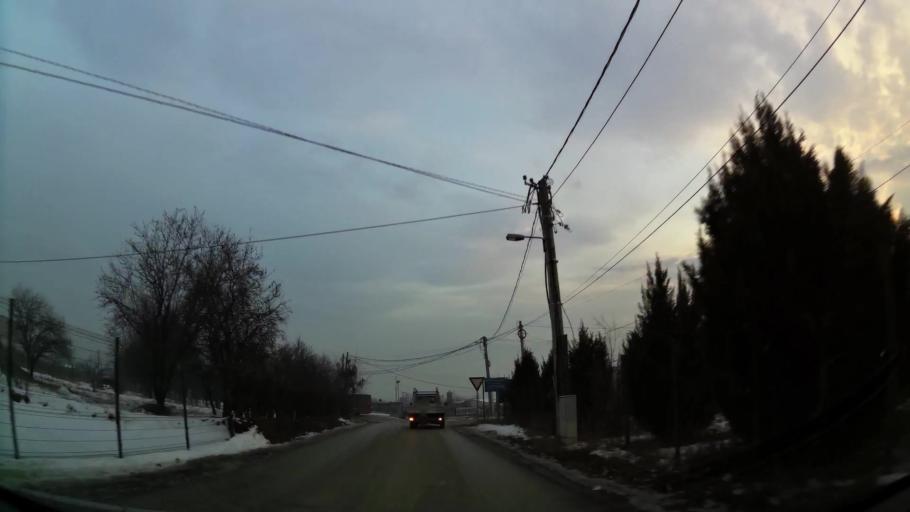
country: MK
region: Suto Orizari
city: Suto Orizare
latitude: 42.0303
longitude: 21.4070
